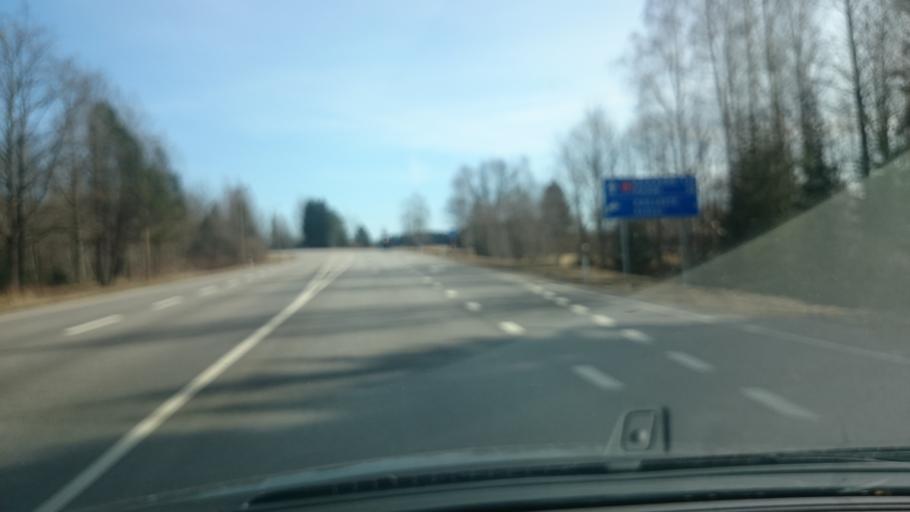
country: EE
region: Paernumaa
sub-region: Vaendra vald (alev)
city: Vandra
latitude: 58.6669
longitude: 25.1461
